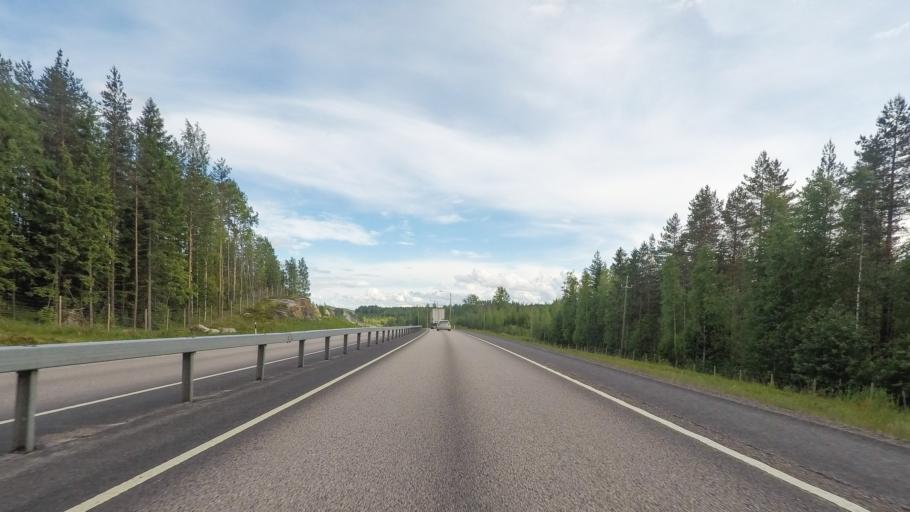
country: FI
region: Central Finland
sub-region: Jyvaeskylae
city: Toivakka
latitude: 62.0154
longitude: 26.0464
